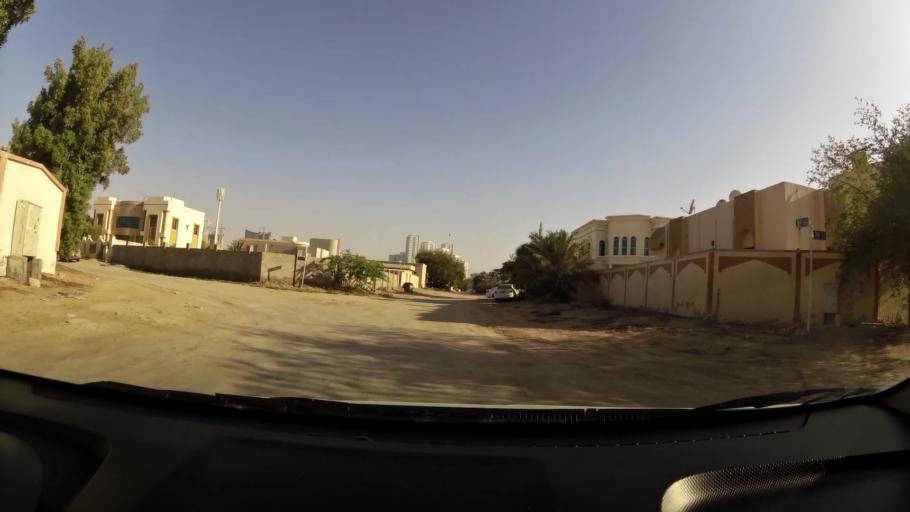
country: AE
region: Ajman
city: Ajman
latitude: 25.4025
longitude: 55.4692
